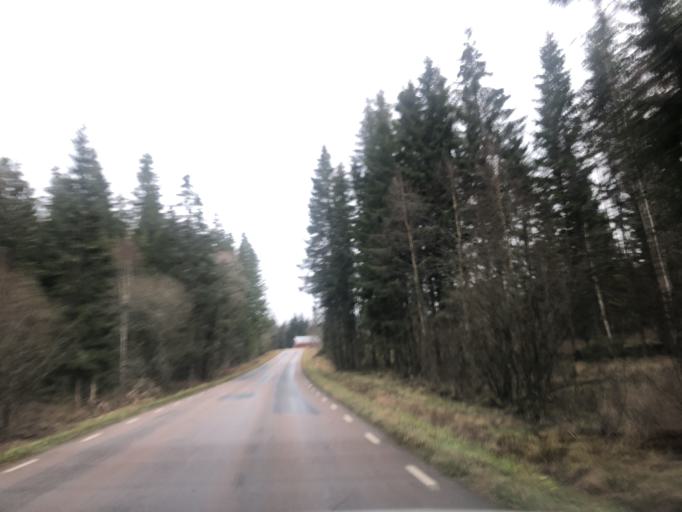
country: SE
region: Vaestra Goetaland
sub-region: Ulricehamns Kommun
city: Ulricehamn
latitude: 57.8311
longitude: 13.4985
